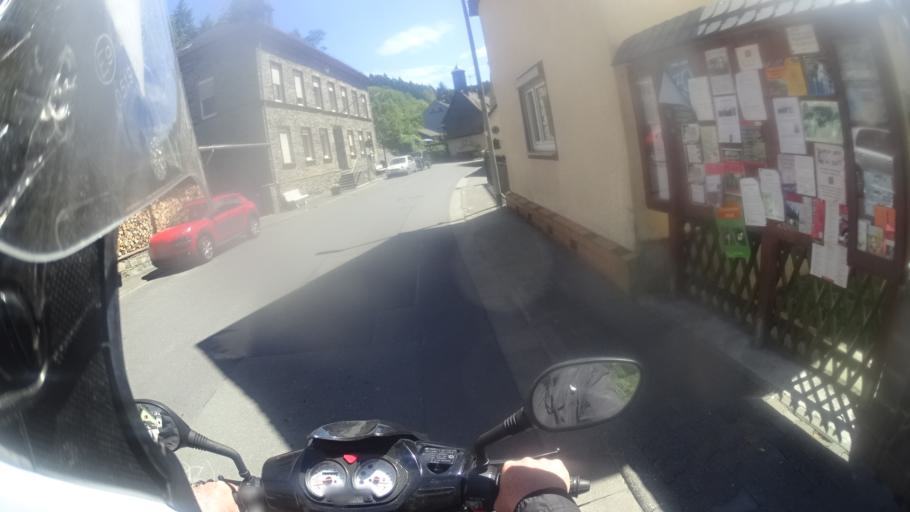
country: DE
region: Hesse
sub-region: Regierungsbezirk Darmstadt
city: Bad Schwalbach
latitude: 50.1068
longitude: 8.0299
